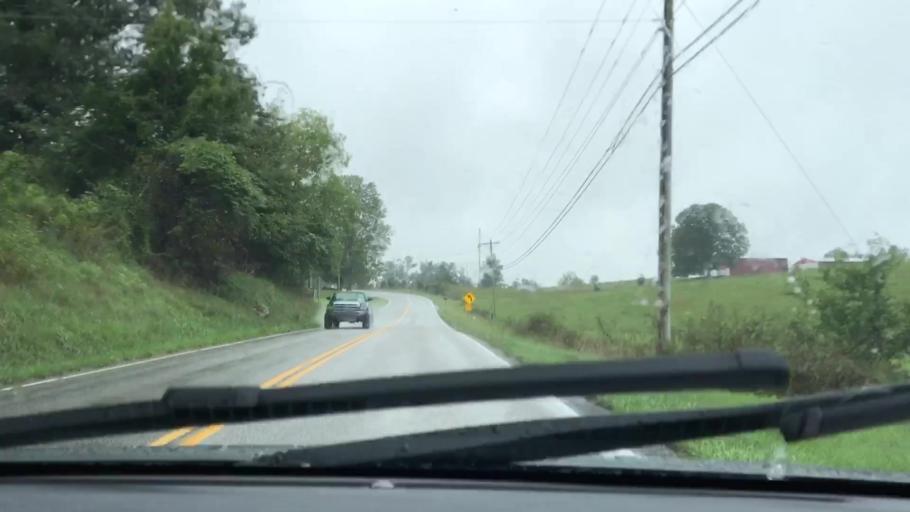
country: US
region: Kentucky
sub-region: Monroe County
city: Tompkinsville
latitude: 36.6904
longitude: -85.7135
